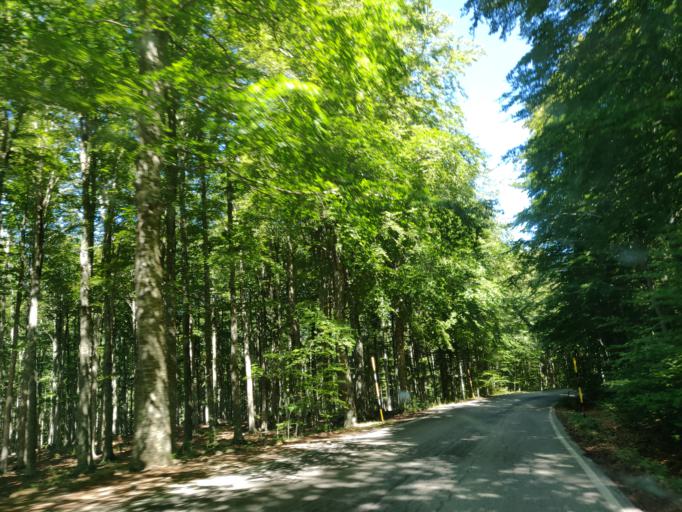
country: IT
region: Tuscany
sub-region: Provincia di Siena
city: Abbadia San Salvatore
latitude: 42.9014
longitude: 11.6165
